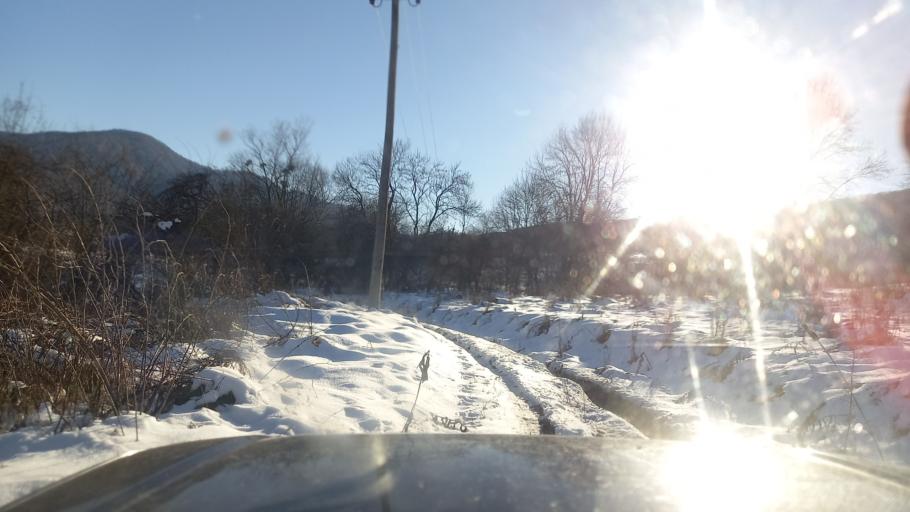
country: RU
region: Adygeya
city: Kamennomostskiy
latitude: 44.2005
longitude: 40.1500
